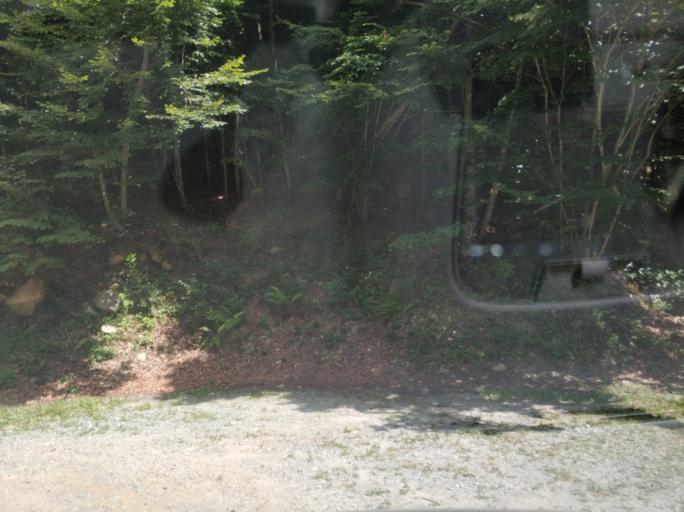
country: IT
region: Piedmont
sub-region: Provincia di Torino
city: Viu
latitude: 45.1996
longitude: 7.3929
